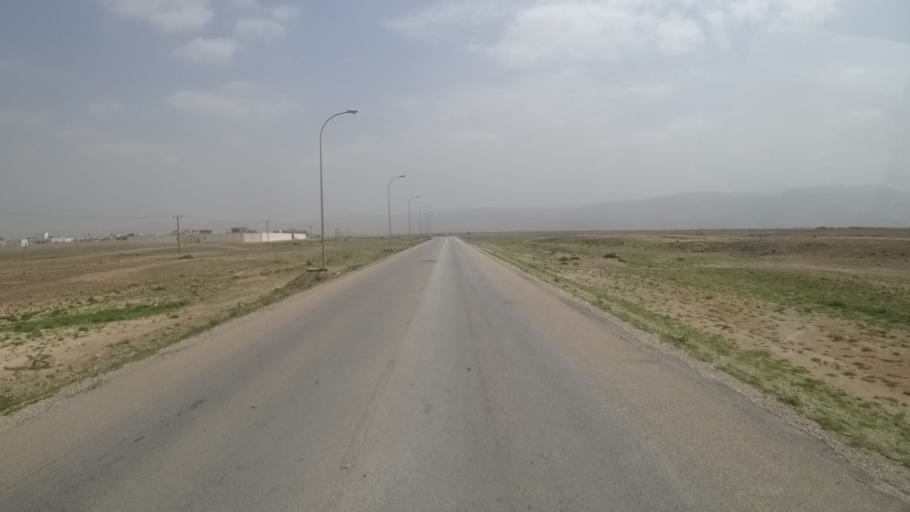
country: OM
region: Zufar
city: Salalah
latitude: 17.0643
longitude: 54.2164
